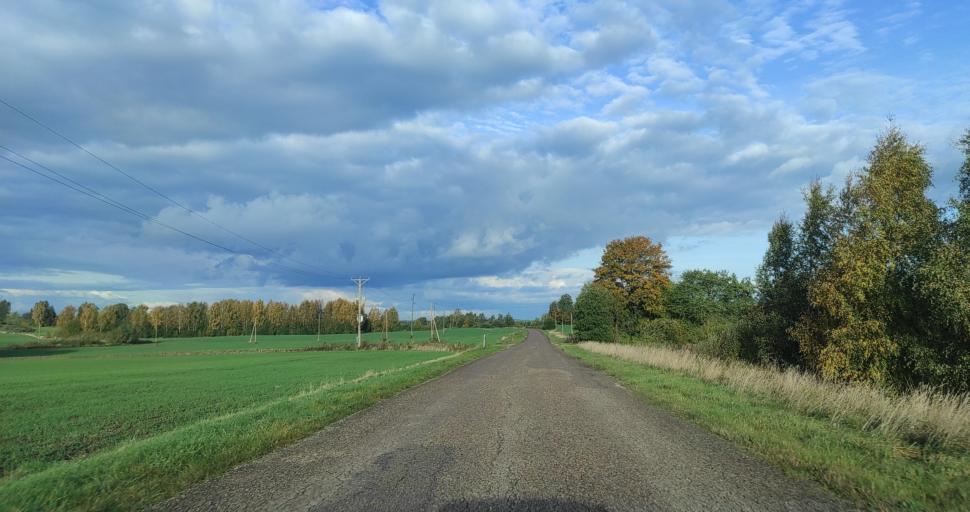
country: LV
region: Aizpute
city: Aizpute
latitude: 56.7774
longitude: 21.7790
